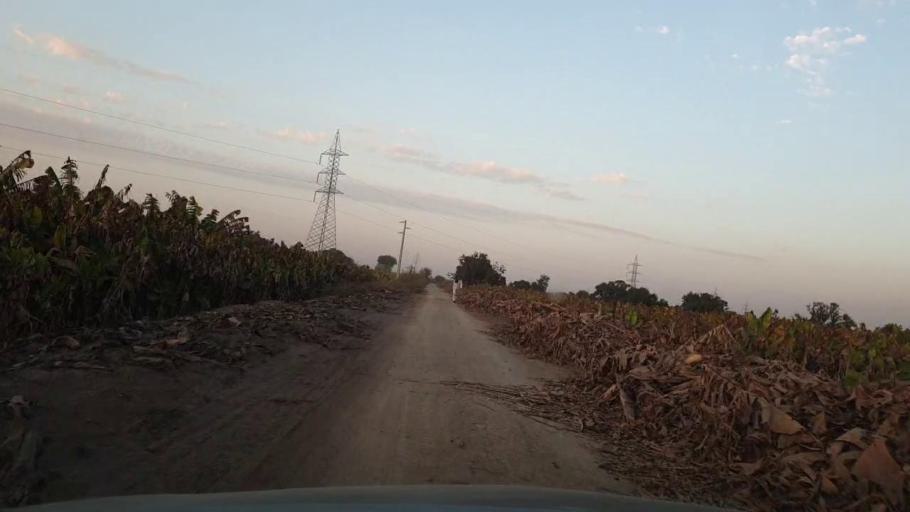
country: PK
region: Sindh
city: Matiari
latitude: 25.6160
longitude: 68.4843
